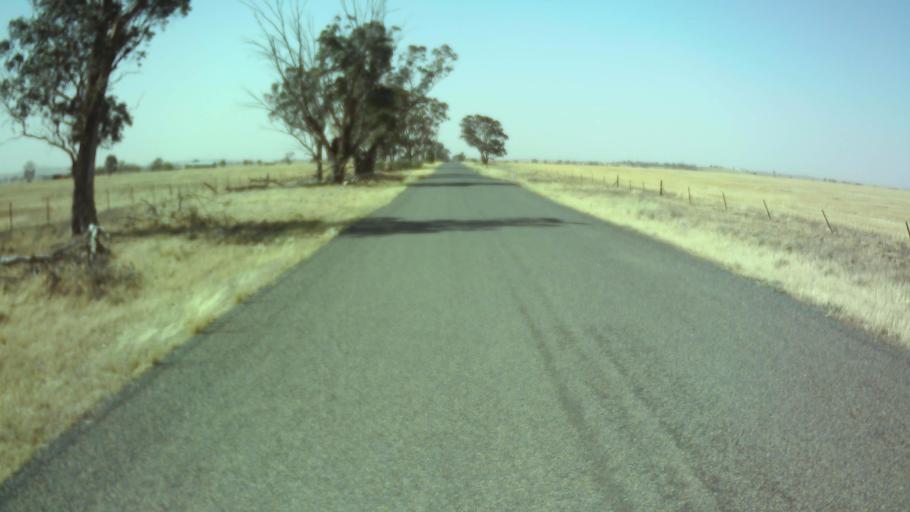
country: AU
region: New South Wales
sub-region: Weddin
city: Grenfell
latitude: -33.8845
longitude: 147.9238
